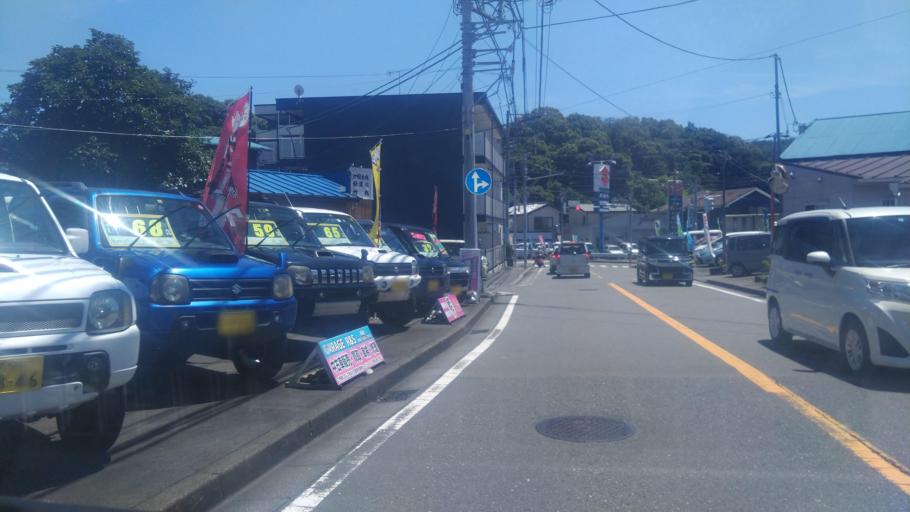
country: JP
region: Kanagawa
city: Fujisawa
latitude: 35.3913
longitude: 139.5098
